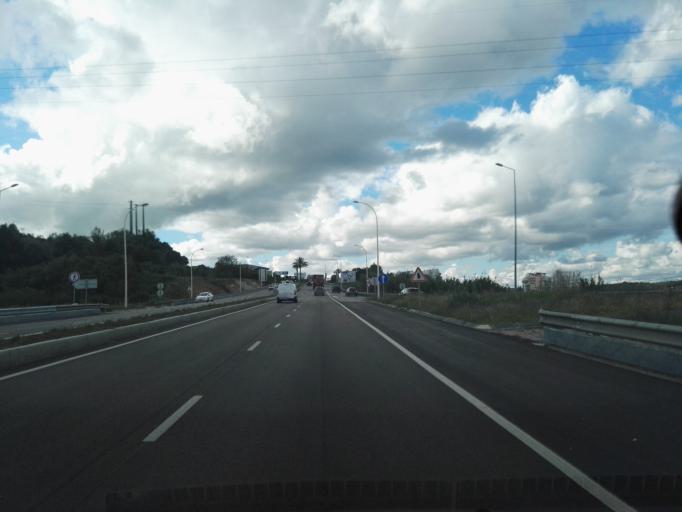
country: PT
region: Santarem
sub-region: Torres Novas
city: Torres Novas
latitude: 39.4661
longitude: -8.5323
